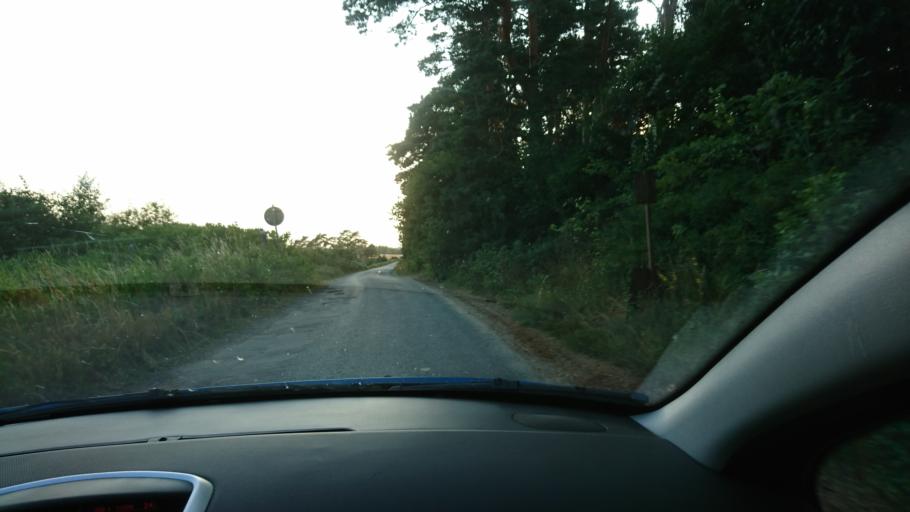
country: SE
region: Skane
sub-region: Simrishamns Kommun
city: Kivik
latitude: 55.7127
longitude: 14.1666
